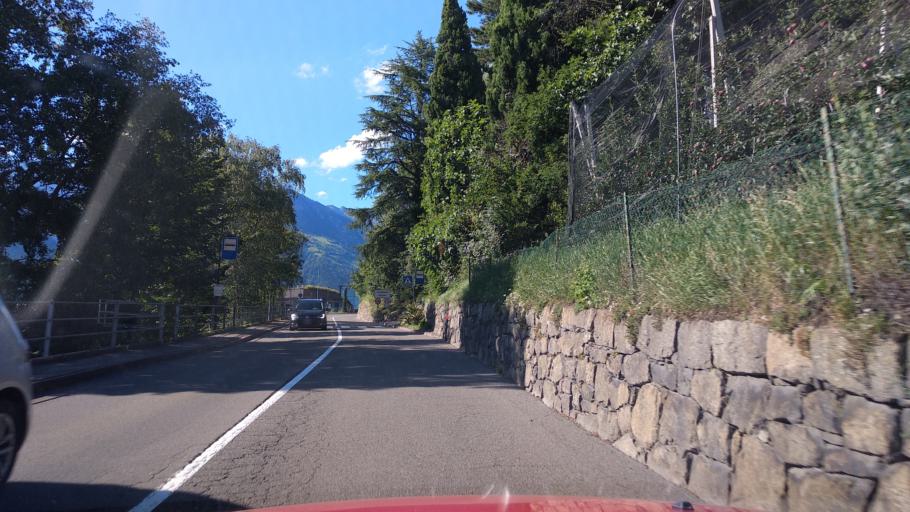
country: IT
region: Trentino-Alto Adige
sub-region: Bolzano
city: Scena
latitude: 46.6746
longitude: 11.1891
